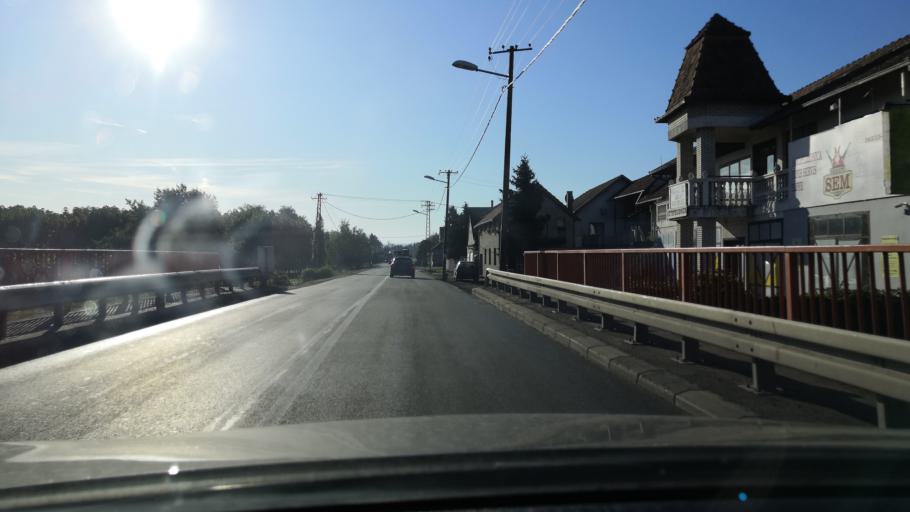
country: RS
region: Autonomna Pokrajina Vojvodina
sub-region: Juznobacki Okrug
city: Petrovaradin
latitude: 45.2344
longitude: 19.8899
